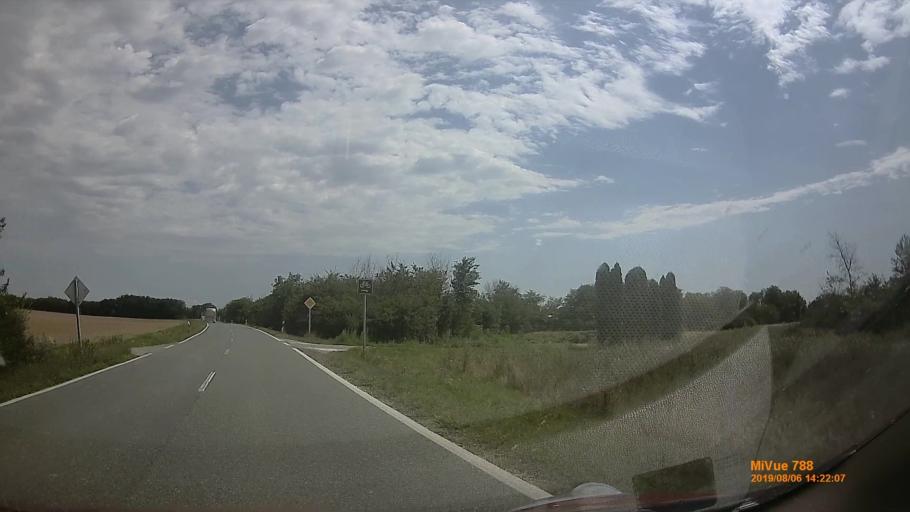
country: HU
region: Vas
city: Vep
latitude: 47.1640
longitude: 16.7855
